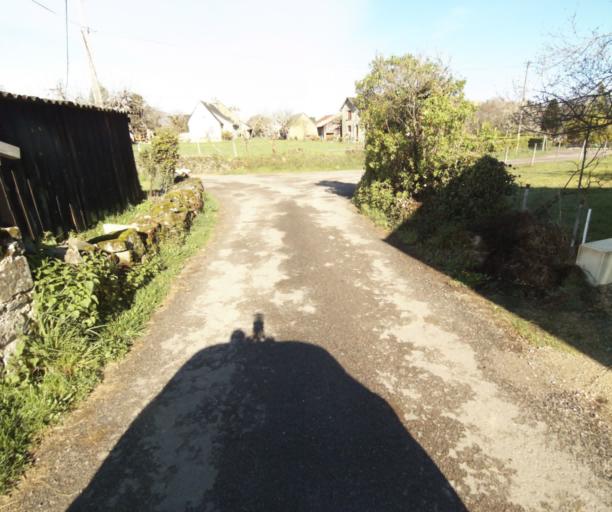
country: FR
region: Limousin
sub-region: Departement de la Correze
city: Laguenne
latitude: 45.2666
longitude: 1.8568
